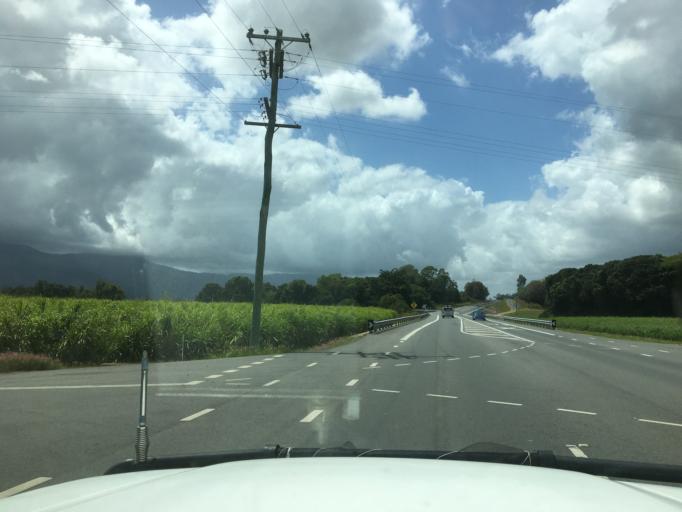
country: AU
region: Queensland
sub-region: Cairns
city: Woree
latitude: -17.1029
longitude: 145.7957
